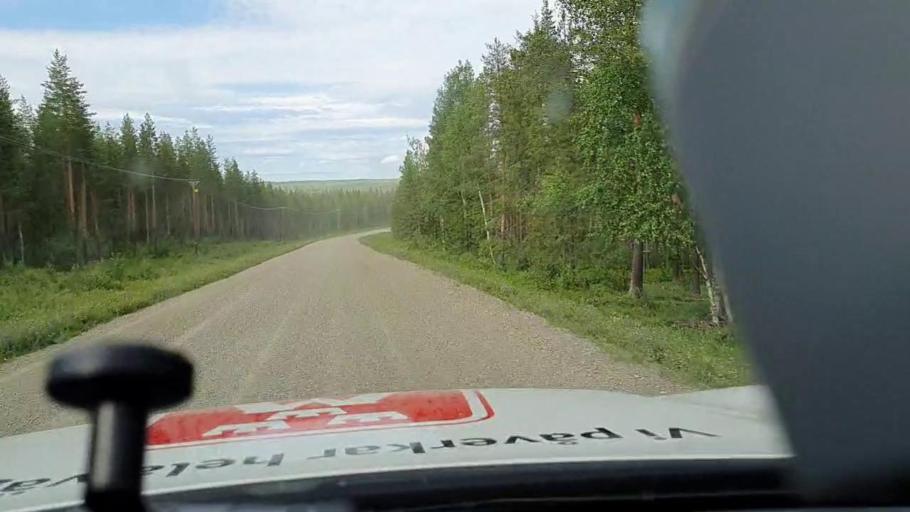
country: SE
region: Norrbotten
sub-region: Alvsbyns Kommun
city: AElvsbyn
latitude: 66.1436
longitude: 21.0188
